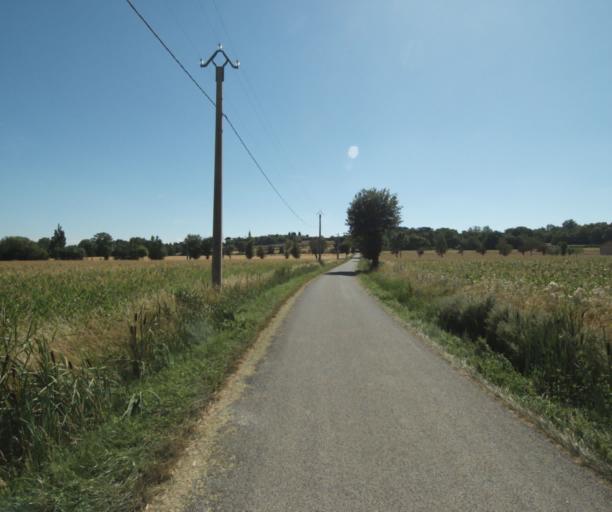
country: FR
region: Midi-Pyrenees
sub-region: Departement de la Haute-Garonne
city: Saint-Felix-Lauragais
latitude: 43.4852
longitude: 1.9280
